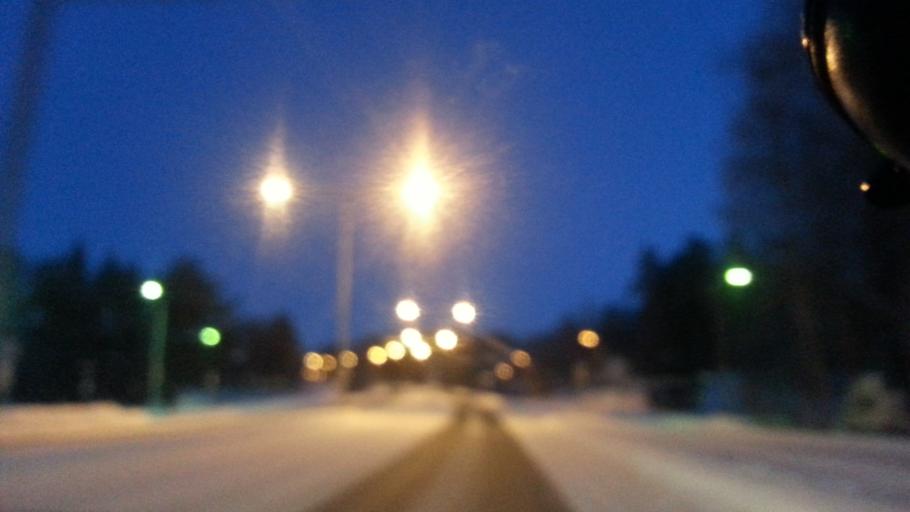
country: FI
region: Lapland
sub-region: Rovaniemi
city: Rovaniemi
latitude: 66.4901
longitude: 25.7559
